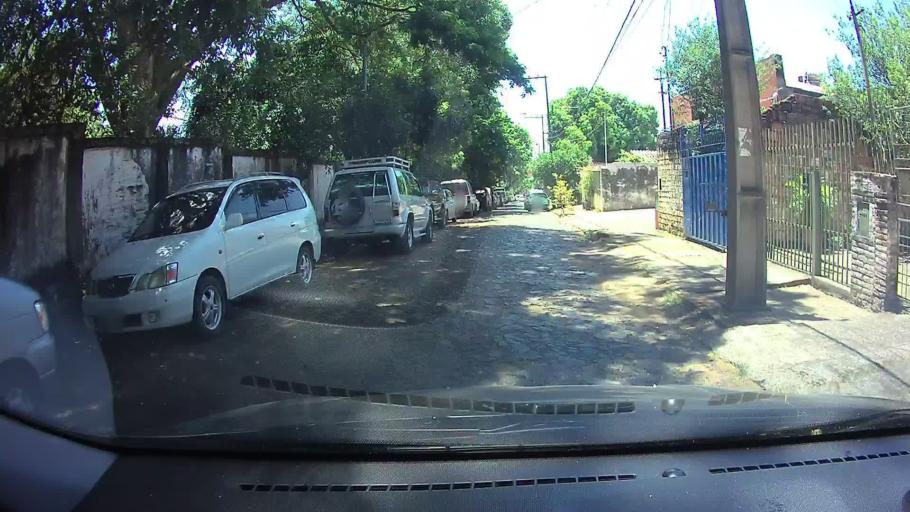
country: PY
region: Central
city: Lambare
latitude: -25.3114
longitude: -57.5950
